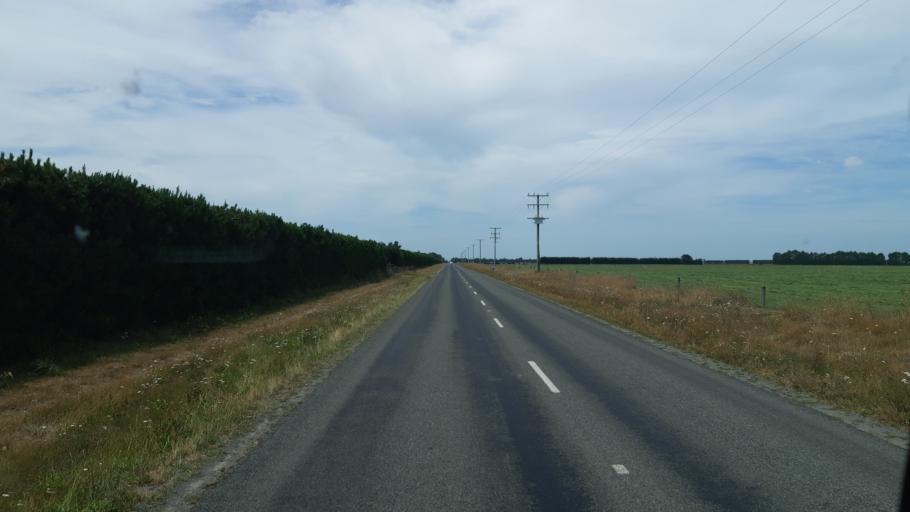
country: NZ
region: Canterbury
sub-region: Ashburton District
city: Tinwald
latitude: -43.9271
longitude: 171.5756
